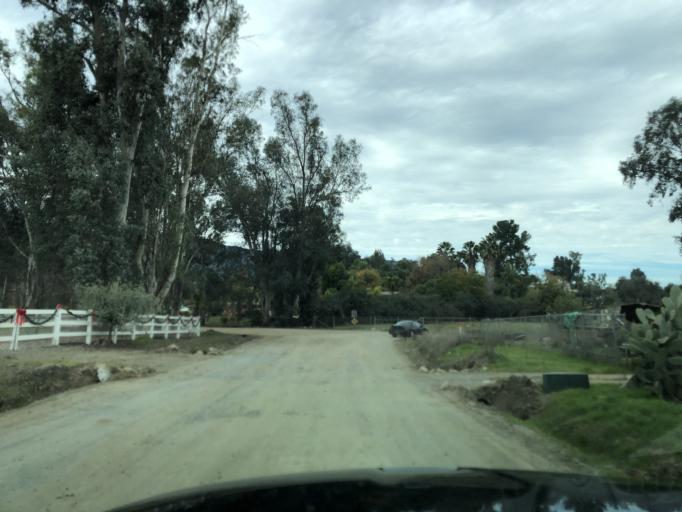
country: US
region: California
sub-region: Riverside County
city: Sedco Hills
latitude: 33.6189
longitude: -117.2910
